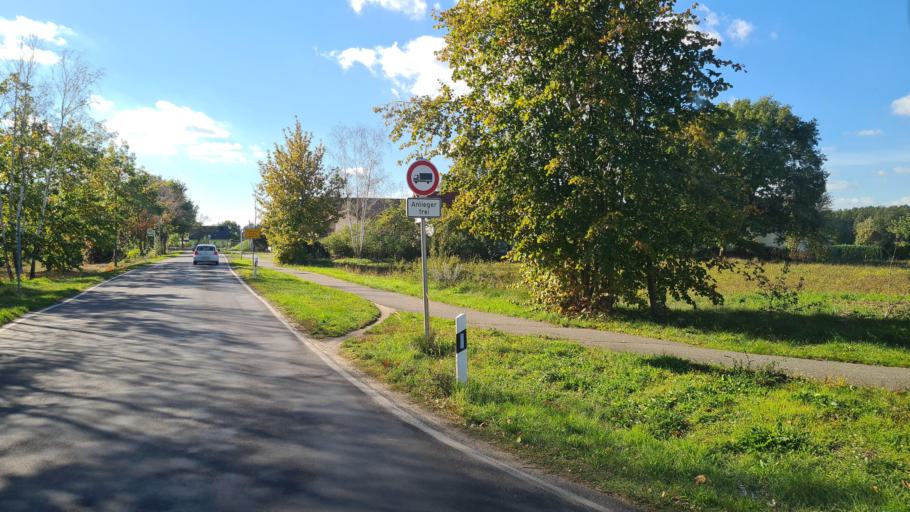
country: DE
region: Brandenburg
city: Kolkwitz
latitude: 51.7654
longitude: 14.2662
